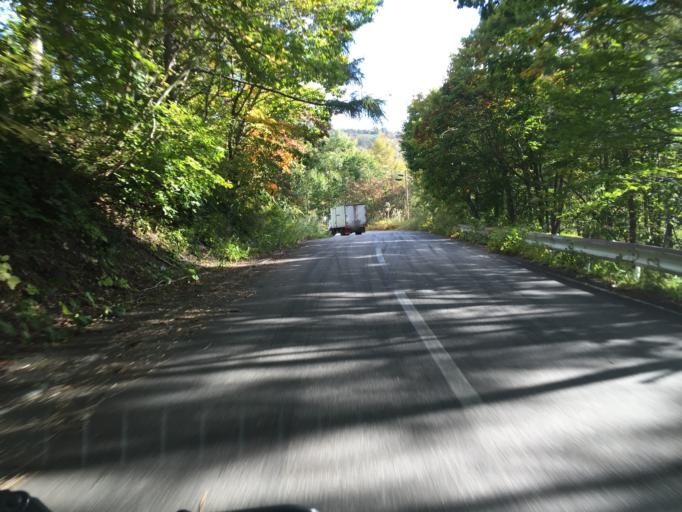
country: JP
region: Fukushima
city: Inawashiro
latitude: 37.6486
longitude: 140.2397
